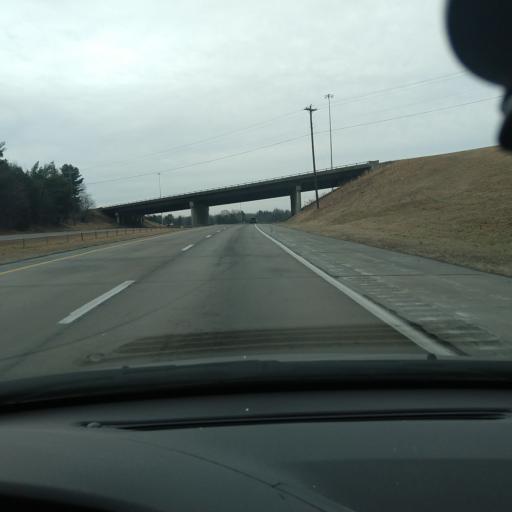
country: US
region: North Carolina
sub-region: Davidson County
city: Midway
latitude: 35.9717
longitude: -80.2302
